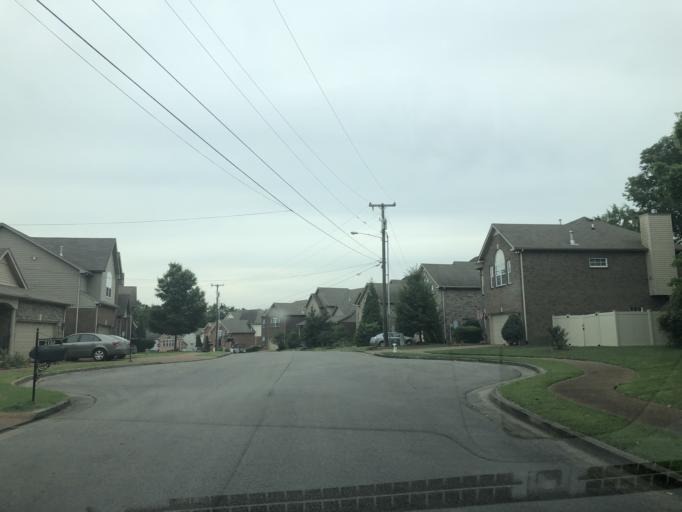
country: US
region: Tennessee
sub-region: Williamson County
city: Nolensville
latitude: 36.0291
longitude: -86.6803
